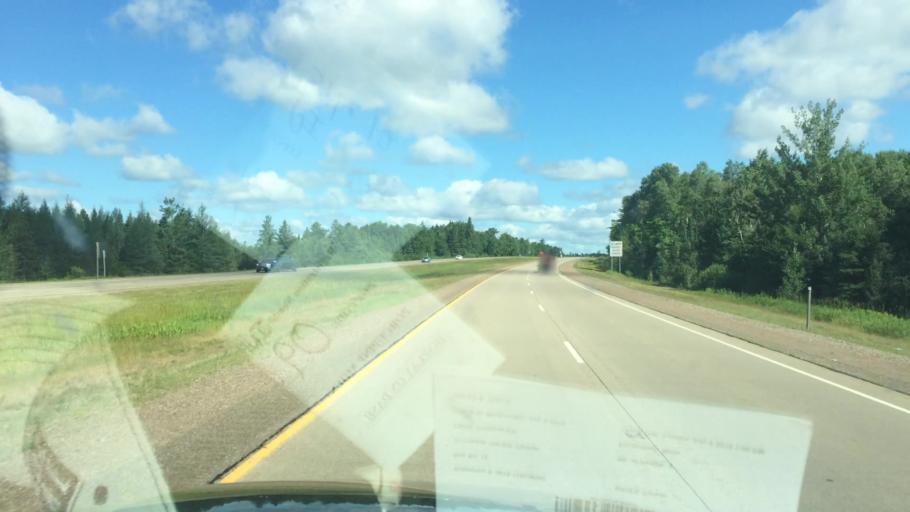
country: US
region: Wisconsin
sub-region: Lincoln County
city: Tomahawk
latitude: 45.4443
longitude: -89.6857
